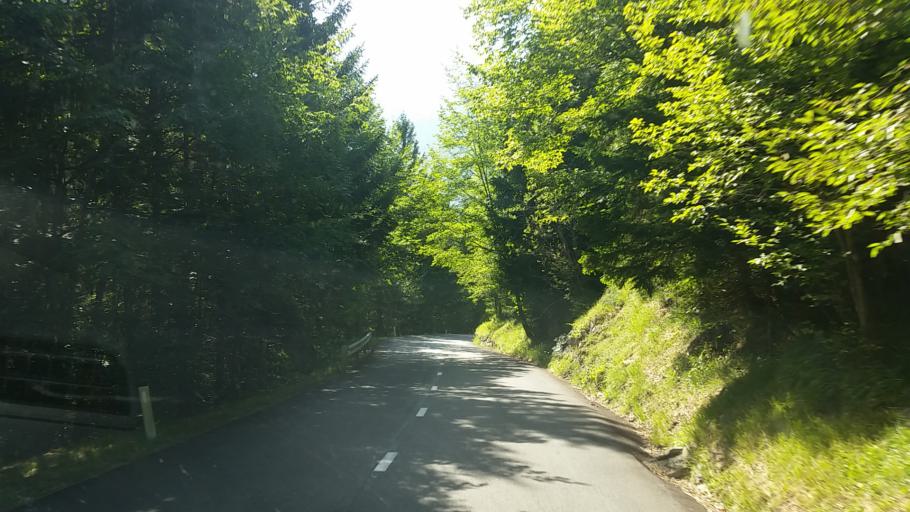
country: SI
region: Kranjska Gora
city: Kranjska Gora
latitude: 46.4068
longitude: 13.7423
